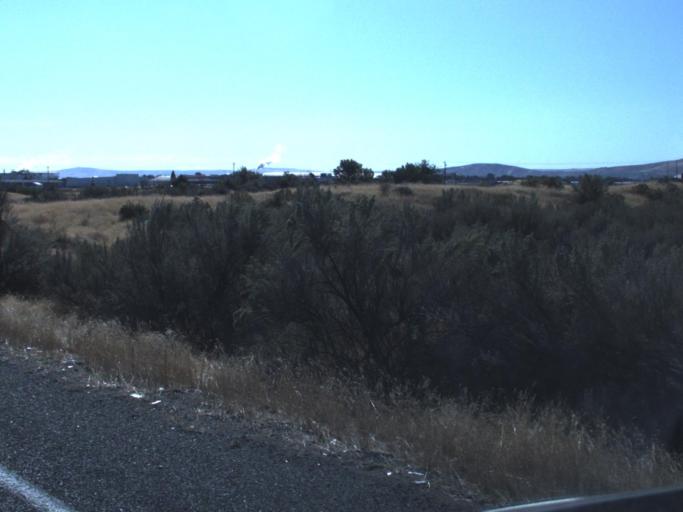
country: US
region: Washington
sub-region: Benton County
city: Richland
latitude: 46.3188
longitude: -119.3029
